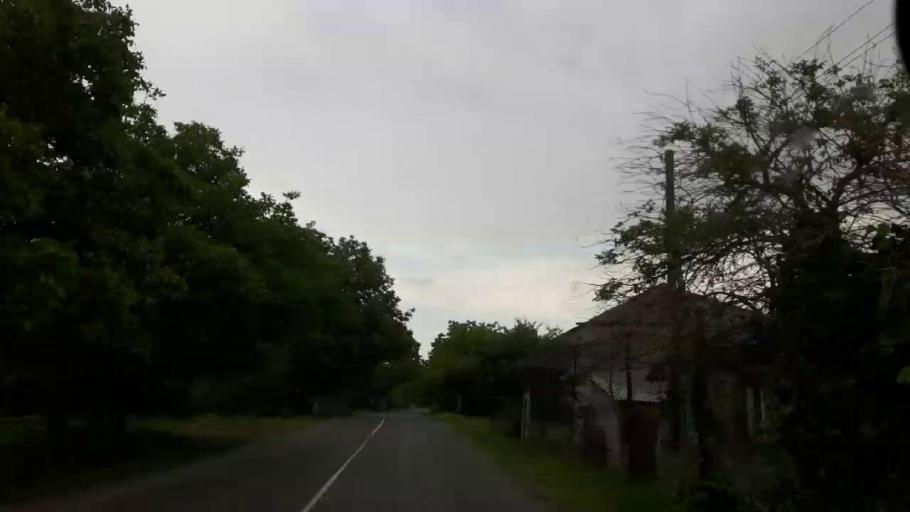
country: GE
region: Shida Kartli
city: Gori
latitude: 41.9595
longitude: 44.2076
